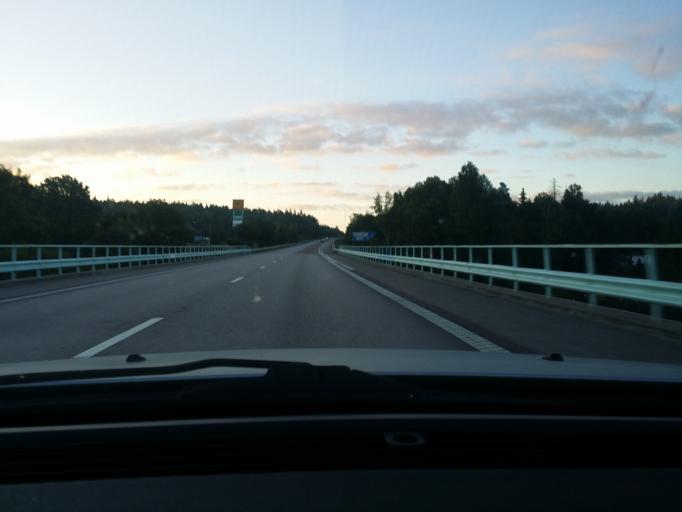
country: SE
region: Uppsala
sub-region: Enkopings Kommun
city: Dalby
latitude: 59.6216
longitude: 17.3871
